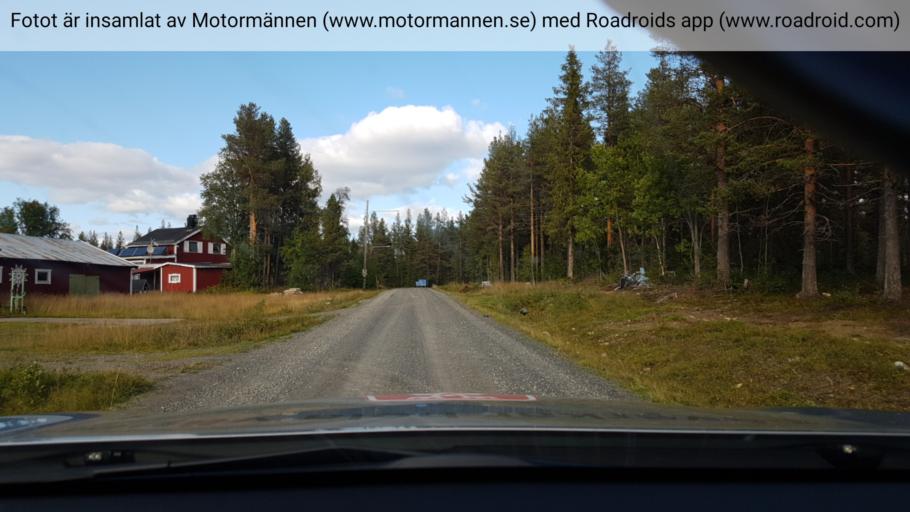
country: SE
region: Vaesterbotten
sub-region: Sorsele Kommun
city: Sorsele
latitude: 65.4589
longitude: 18.1400
